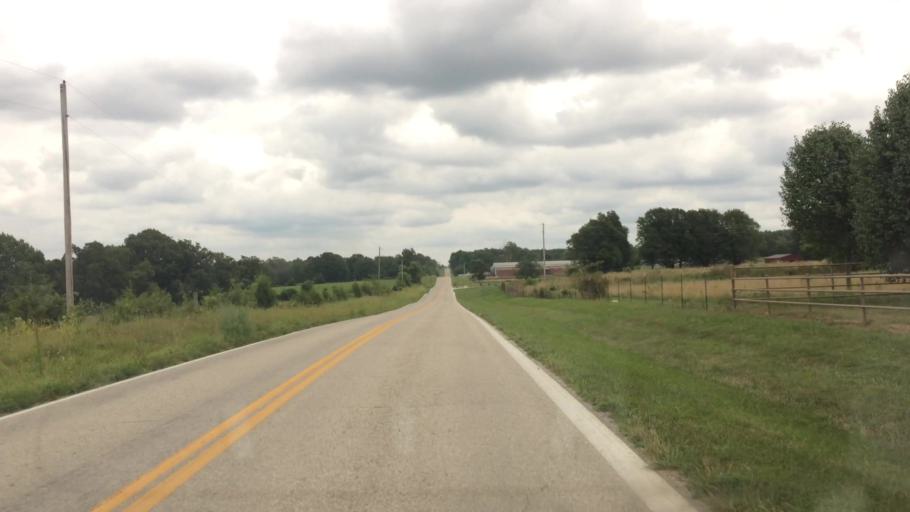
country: US
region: Missouri
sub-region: Greene County
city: Strafford
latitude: 37.3005
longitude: -93.1658
